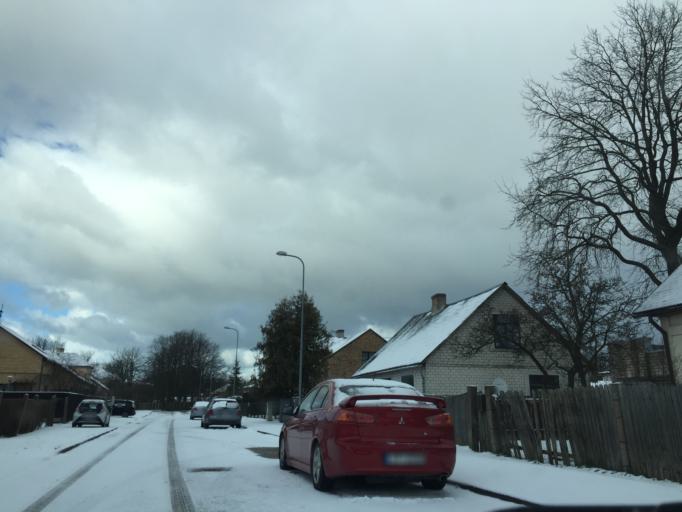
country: LV
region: Ventspils
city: Ventspils
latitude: 57.3851
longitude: 21.5645
